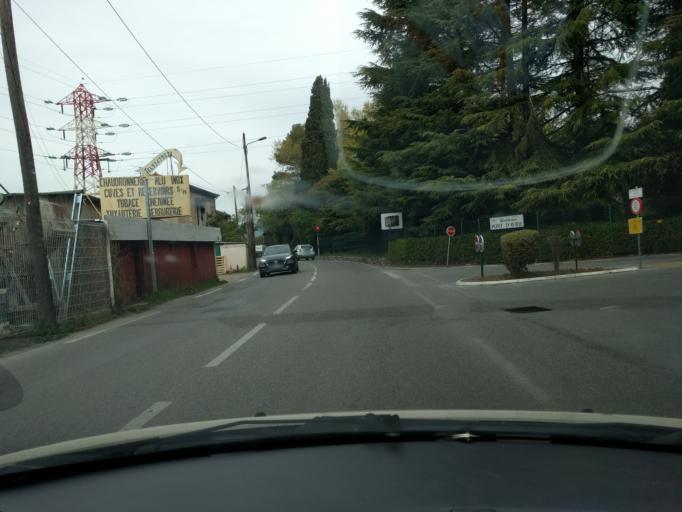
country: FR
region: Provence-Alpes-Cote d'Azur
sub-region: Departement des Alpes-Maritimes
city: La Roquette-sur-Siagne
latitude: 43.5729
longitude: 6.9533
